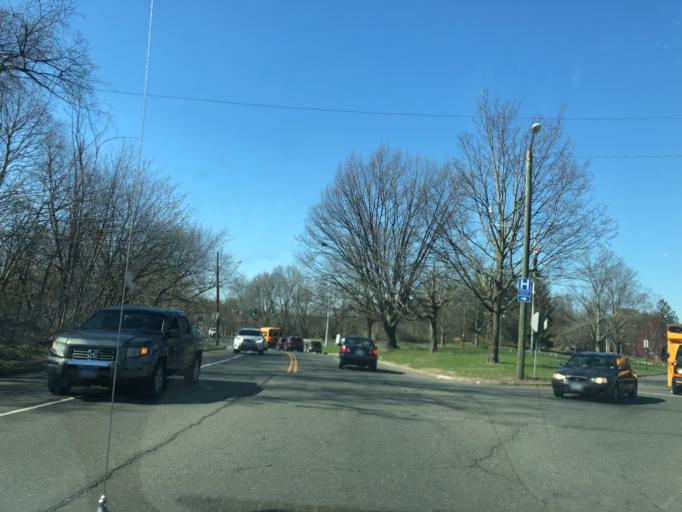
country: US
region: Connecticut
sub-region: Hartford County
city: Hartford
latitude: 41.7406
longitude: -72.6930
